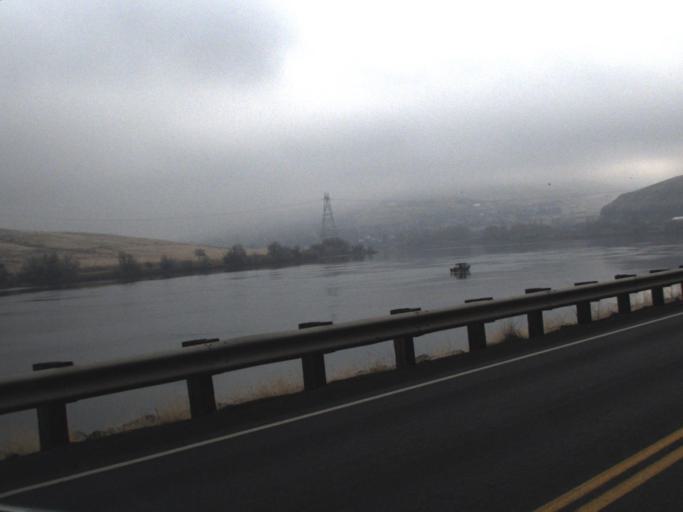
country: US
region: Washington
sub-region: Asotin County
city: Asotin
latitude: 46.3545
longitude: -117.0642
